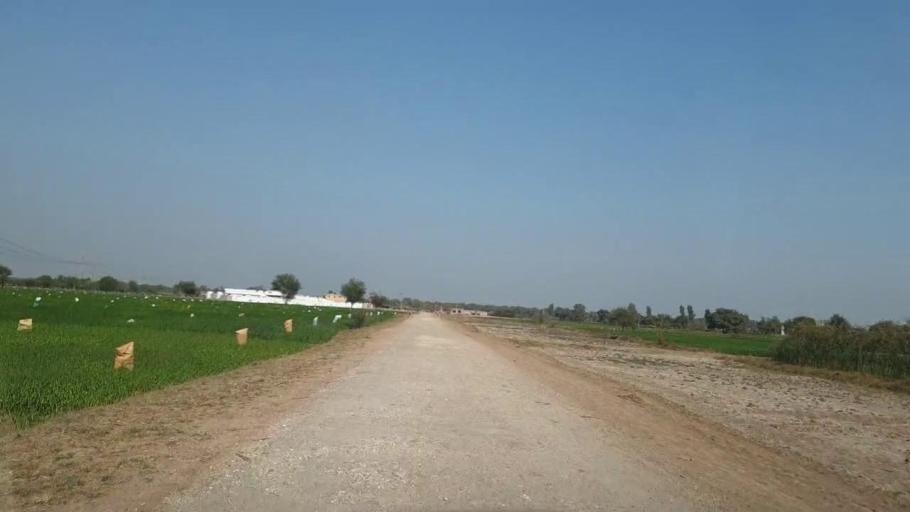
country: PK
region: Sindh
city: Matiari
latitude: 25.5040
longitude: 68.4575
